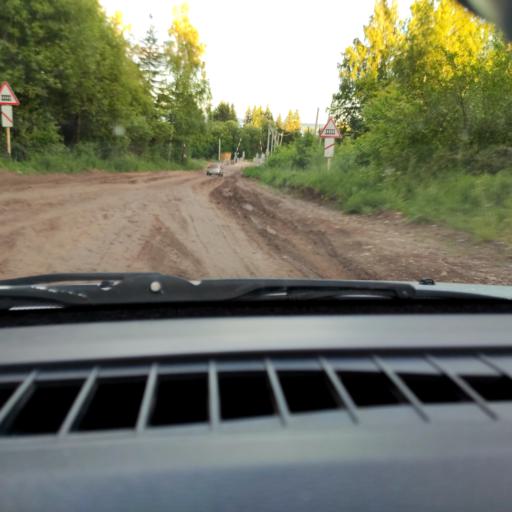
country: RU
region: Perm
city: Polazna
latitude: 58.1982
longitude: 56.4754
